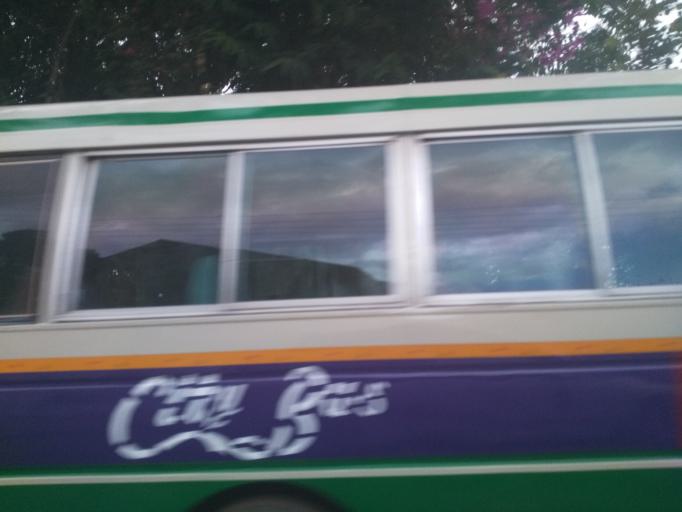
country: TZ
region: Dar es Salaam
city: Magomeni
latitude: -6.7949
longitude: 39.2732
